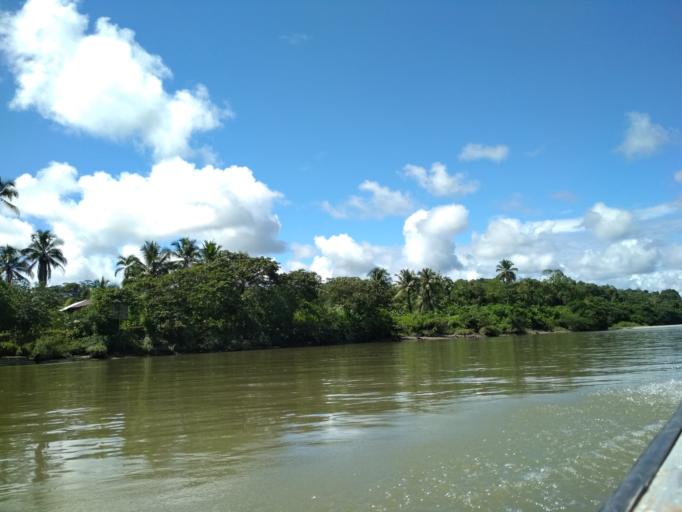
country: CO
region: Cauca
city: Timbiqui
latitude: 2.7640
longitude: -77.6633
